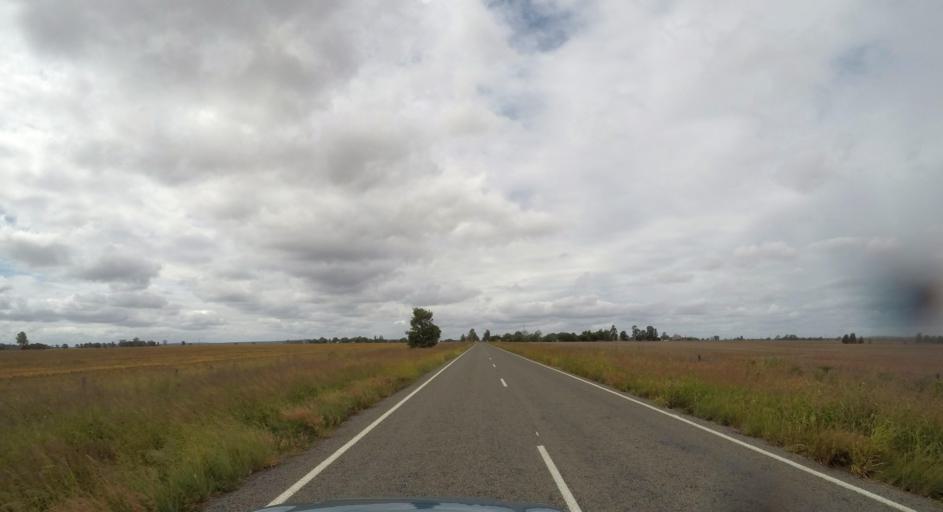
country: AU
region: Queensland
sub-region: South Burnett
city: Kingaroy
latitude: -26.3939
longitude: 151.2335
